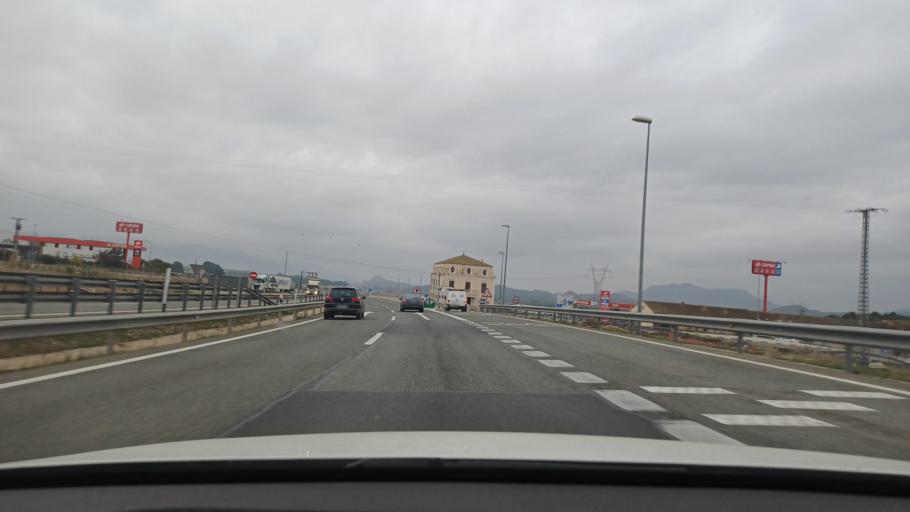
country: ES
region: Valencia
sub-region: Provincia de Alicante
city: Sax
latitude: 38.5749
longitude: -0.8409
